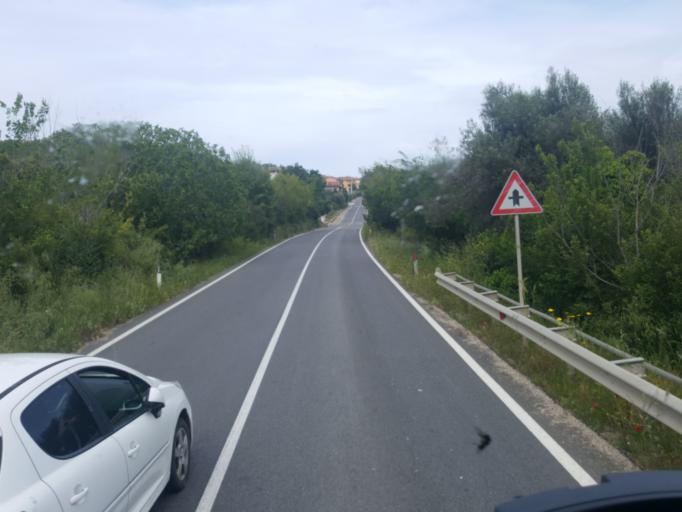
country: IT
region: Latium
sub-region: Provincia di Viterbo
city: Monte Romano
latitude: 42.2671
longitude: 11.8874
